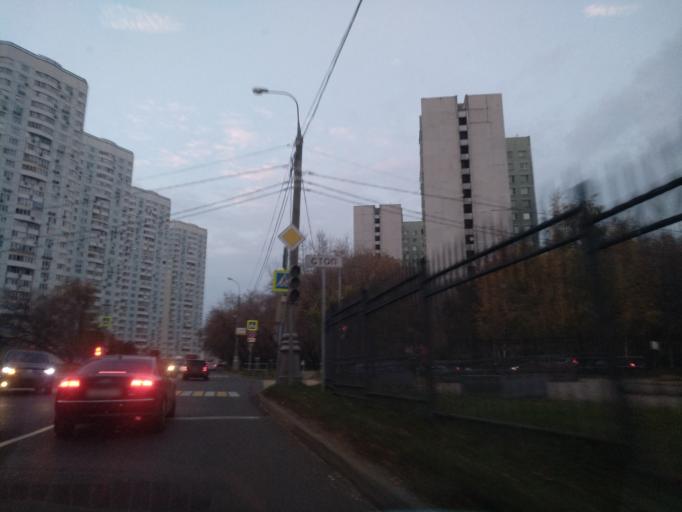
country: RU
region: Moscow
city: Sviblovo
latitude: 55.8666
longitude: 37.6411
